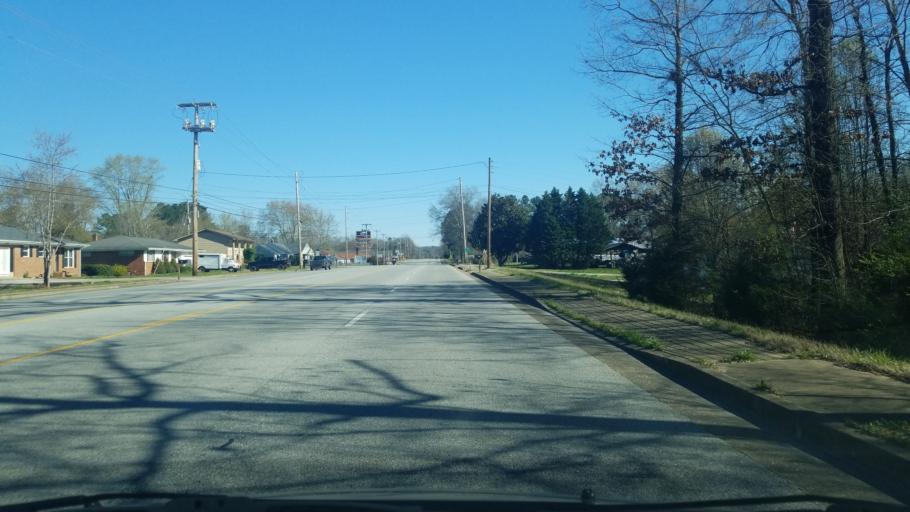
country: US
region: Tennessee
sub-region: Hamilton County
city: Middle Valley
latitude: 35.1849
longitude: -85.1686
